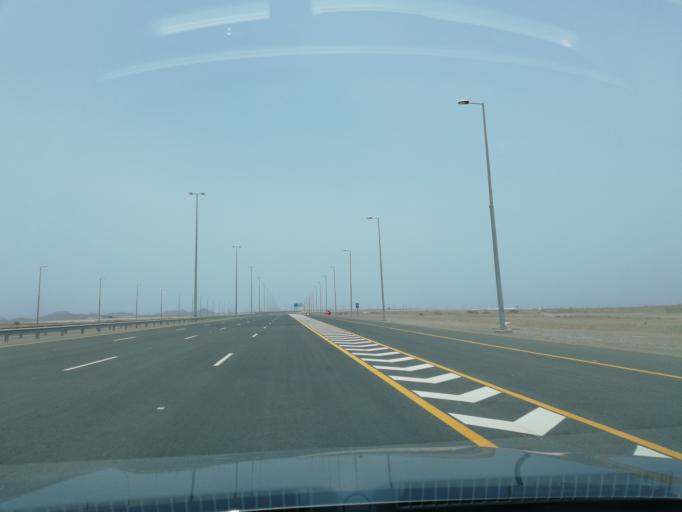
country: OM
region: Al Batinah
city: Al Liwa'
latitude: 24.4443
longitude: 56.5206
